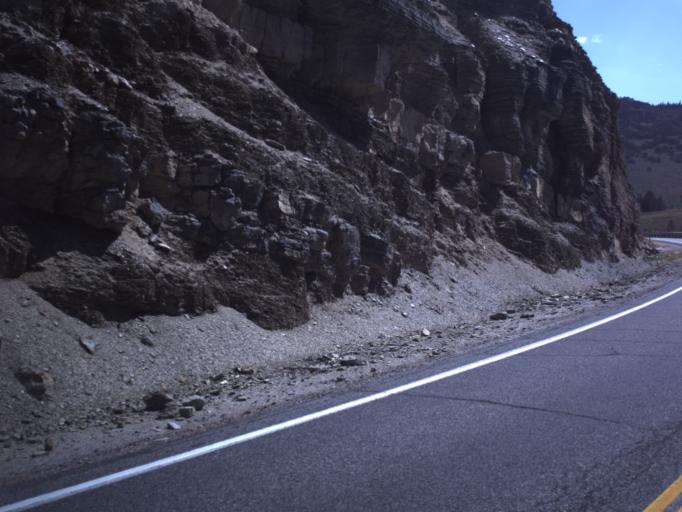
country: US
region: Idaho
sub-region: Bear Lake County
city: Paris
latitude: 41.9517
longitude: -111.4951
